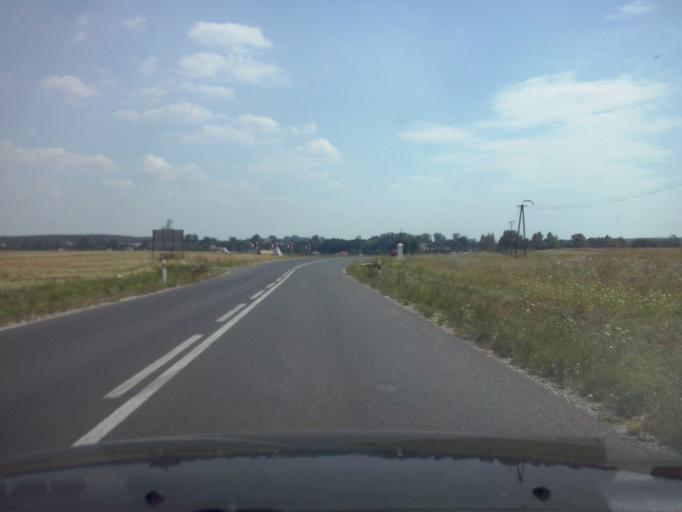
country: PL
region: Swietokrzyskie
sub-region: Powiat buski
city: Gnojno
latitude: 50.5972
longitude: 20.8742
